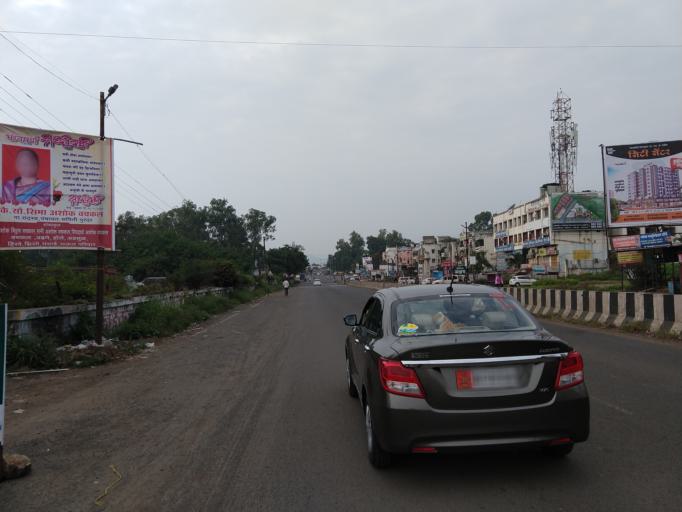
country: IN
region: Maharashtra
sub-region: Pune Division
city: Sasvad
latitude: 18.3520
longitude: 74.0288
